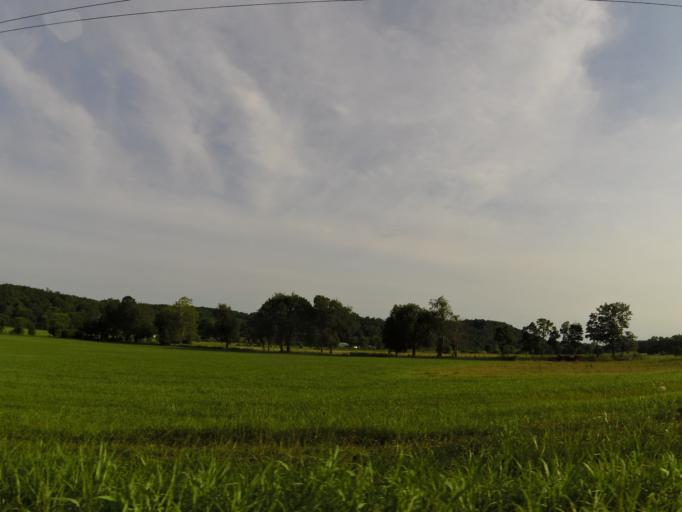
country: US
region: Tennessee
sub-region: Humphreys County
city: McEwen
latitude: 36.0972
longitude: -87.5906
